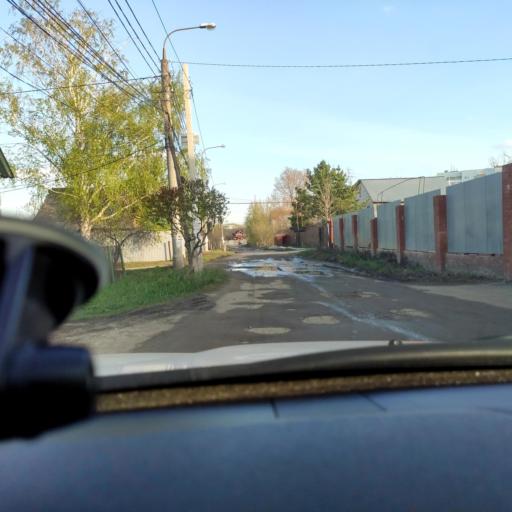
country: RU
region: Samara
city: Volzhskiy
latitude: 53.3540
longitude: 50.2143
